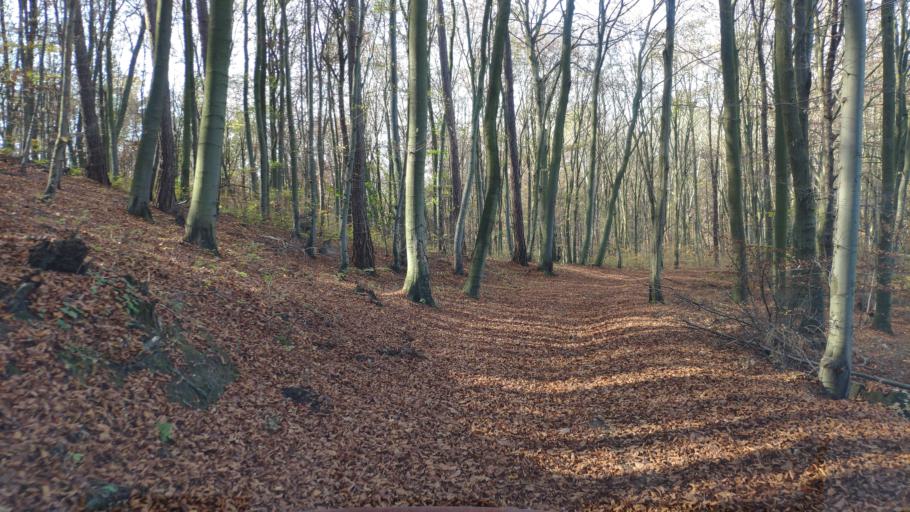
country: SK
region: Presovsky
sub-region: Okres Presov
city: Presov
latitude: 48.8985
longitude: 21.2236
